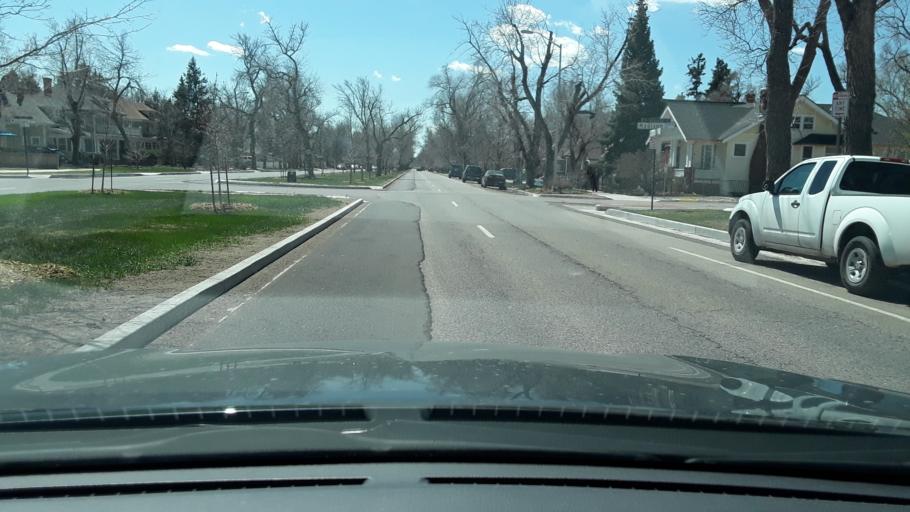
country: US
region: Colorado
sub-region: El Paso County
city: Colorado Springs
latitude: 38.8647
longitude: -104.8202
